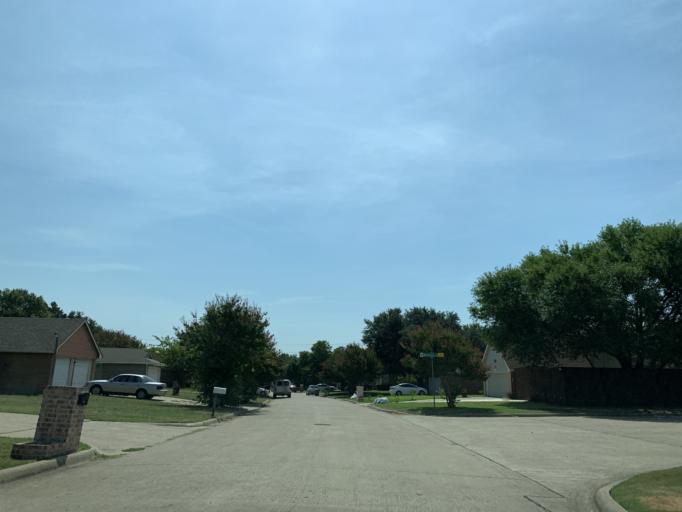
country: US
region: Texas
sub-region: Dallas County
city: Grand Prairie
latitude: 32.6673
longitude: -97.0410
